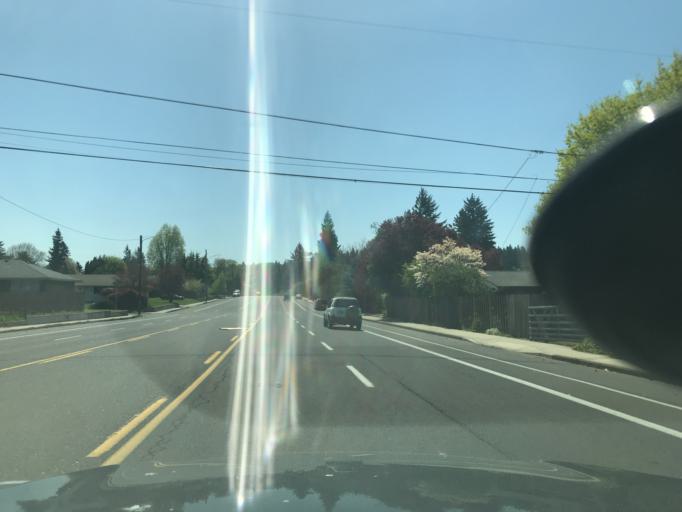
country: US
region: Oregon
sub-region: Clackamas County
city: Happy Valley
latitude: 45.5027
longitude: -122.4969
